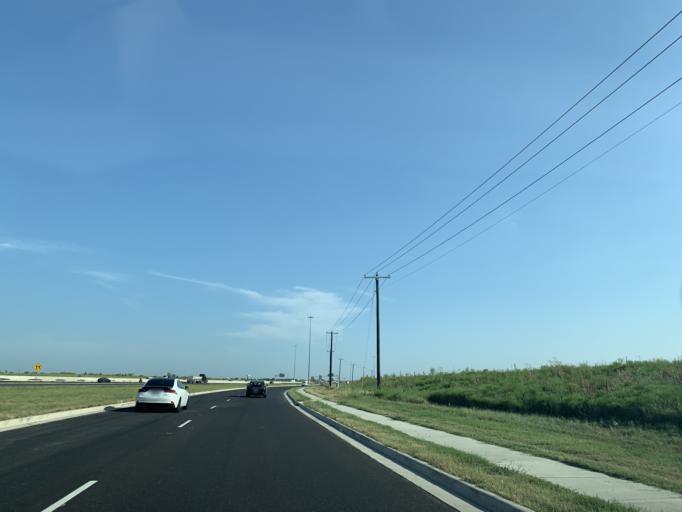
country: US
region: Texas
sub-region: Tarrant County
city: Blue Mound
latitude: 32.8873
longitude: -97.3158
